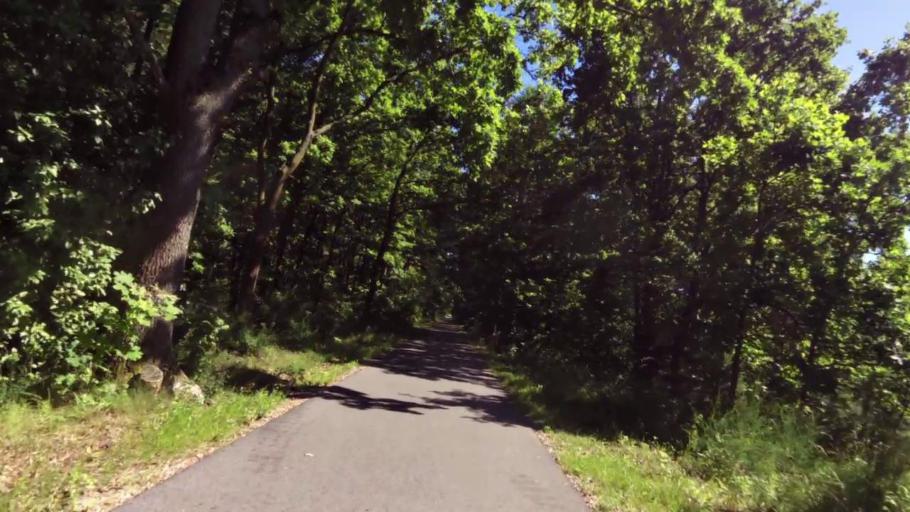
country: PL
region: West Pomeranian Voivodeship
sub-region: Powiat bialogardzki
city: Karlino
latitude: 54.0498
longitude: 15.8784
